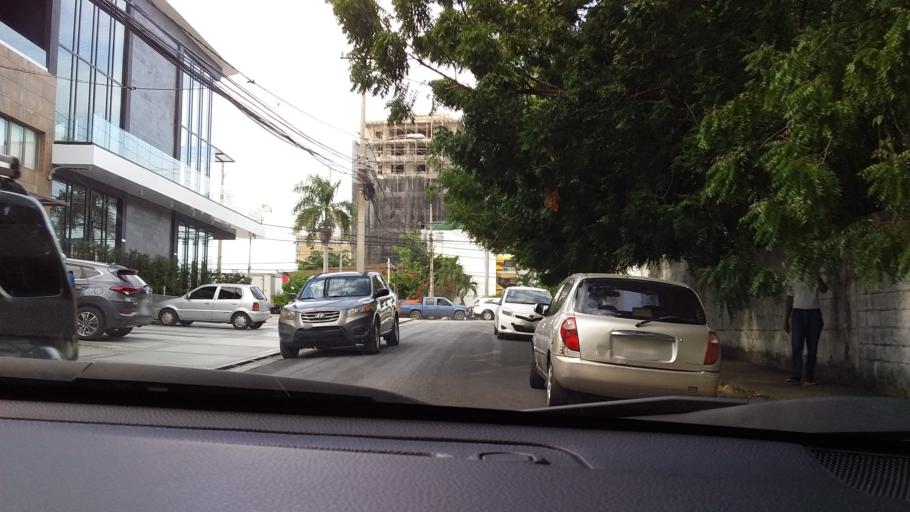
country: DO
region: Nacional
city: La Julia
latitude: 18.4575
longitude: -69.9335
